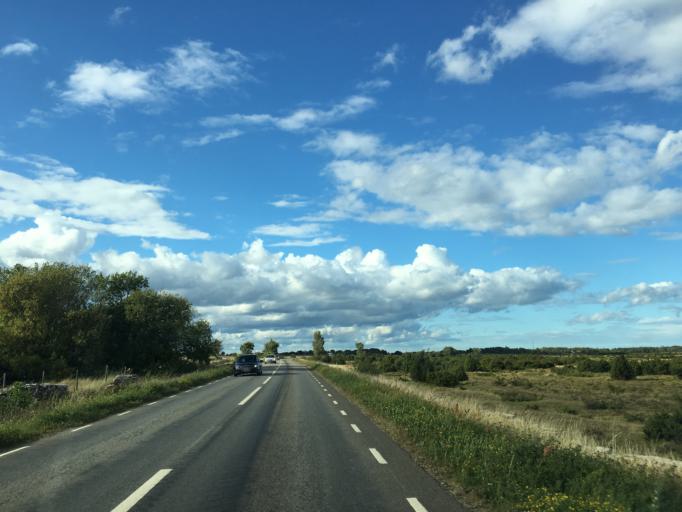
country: SE
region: Kalmar
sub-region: Morbylanga Kommun
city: Moerbylanga
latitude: 56.4935
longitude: 16.4261
